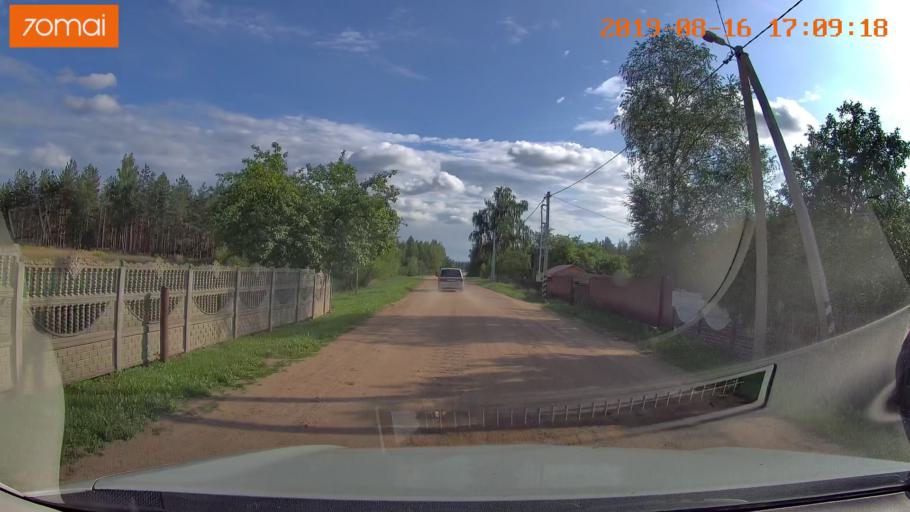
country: BY
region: Mogilev
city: Hlusha
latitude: 53.2146
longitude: 28.9251
